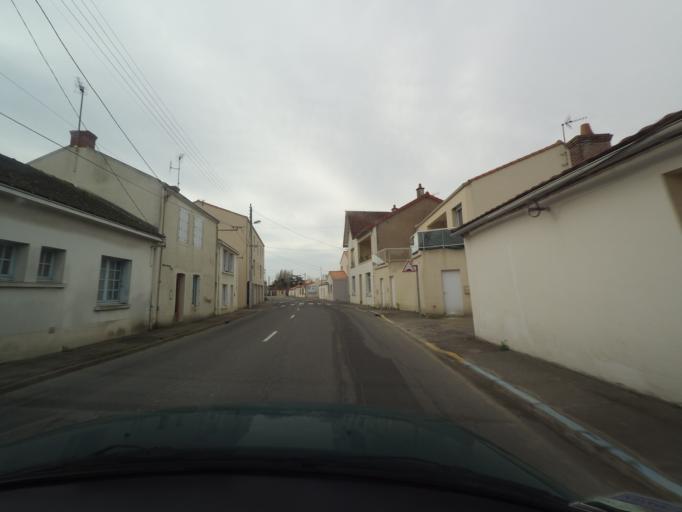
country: FR
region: Pays de la Loire
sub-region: Departement de la Loire-Atlantique
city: Arthon-en-Retz
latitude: 47.1167
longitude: -1.9437
